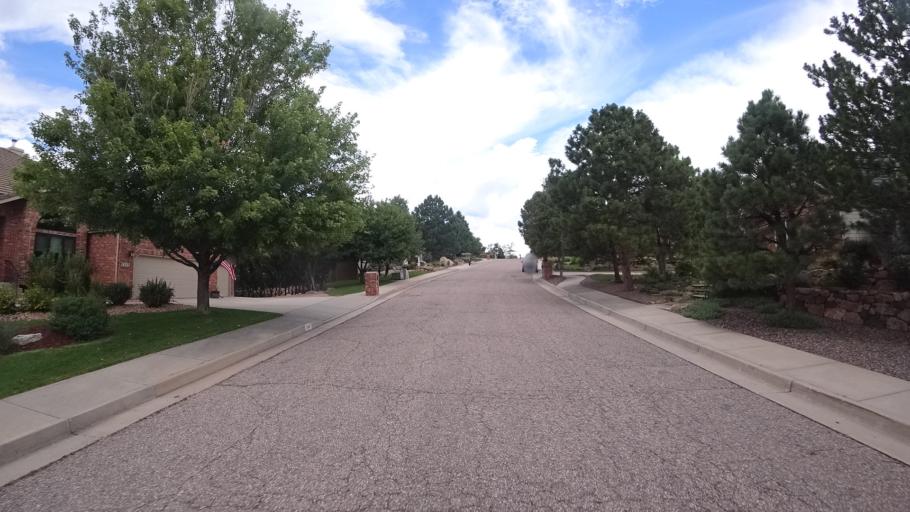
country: US
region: Colorado
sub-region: El Paso County
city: Colorado Springs
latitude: 38.9079
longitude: -104.8511
